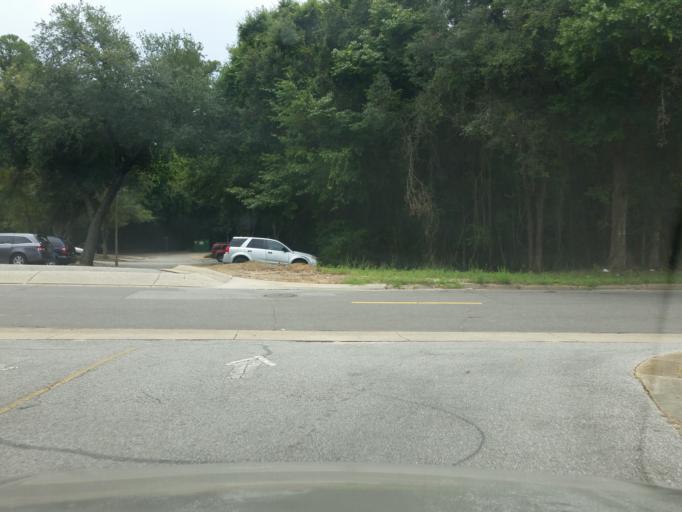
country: US
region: Florida
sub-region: Escambia County
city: Brent
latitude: 30.4717
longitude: -87.2115
